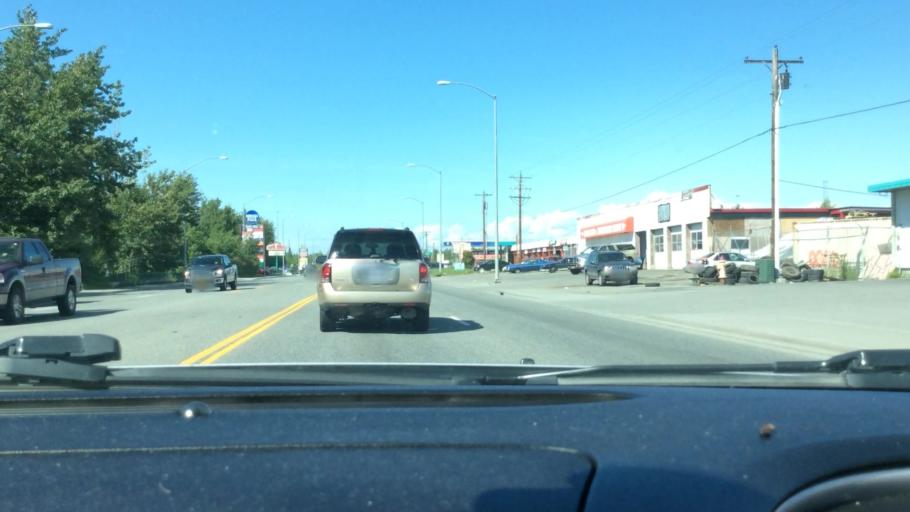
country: US
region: Alaska
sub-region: Anchorage Municipality
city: Anchorage
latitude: 61.2193
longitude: -149.7785
